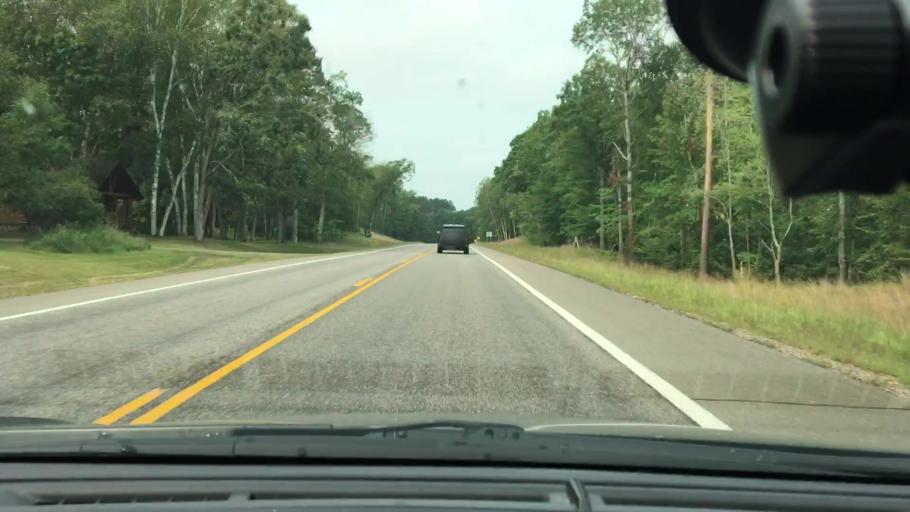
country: US
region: Minnesota
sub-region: Crow Wing County
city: Cross Lake
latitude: 46.6603
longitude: -94.0927
